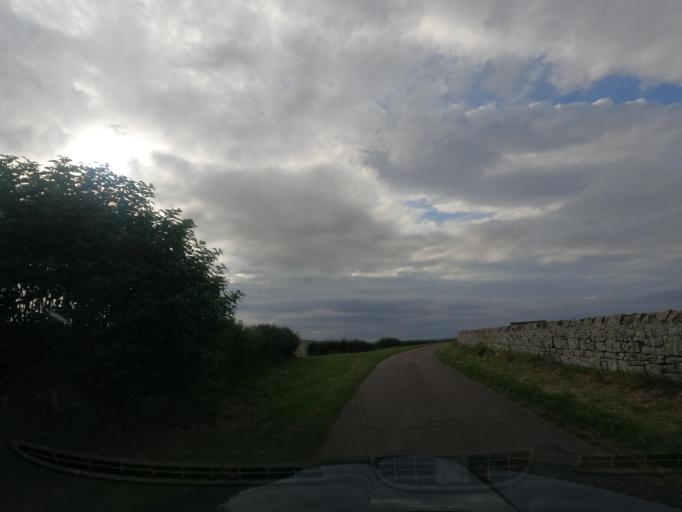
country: GB
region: England
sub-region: Northumberland
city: Ancroft
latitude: 55.7185
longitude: -2.0537
